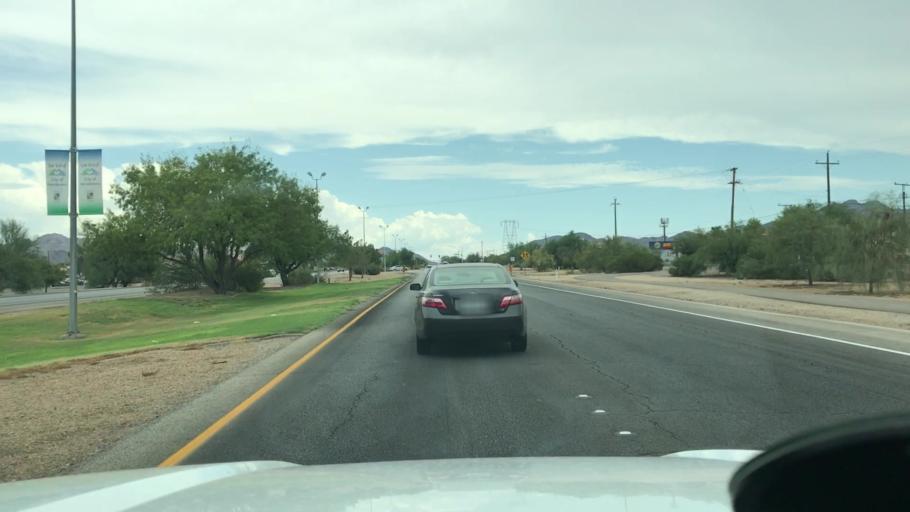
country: US
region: Nevada
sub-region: Clark County
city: Henderson
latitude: 36.0273
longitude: -114.9684
